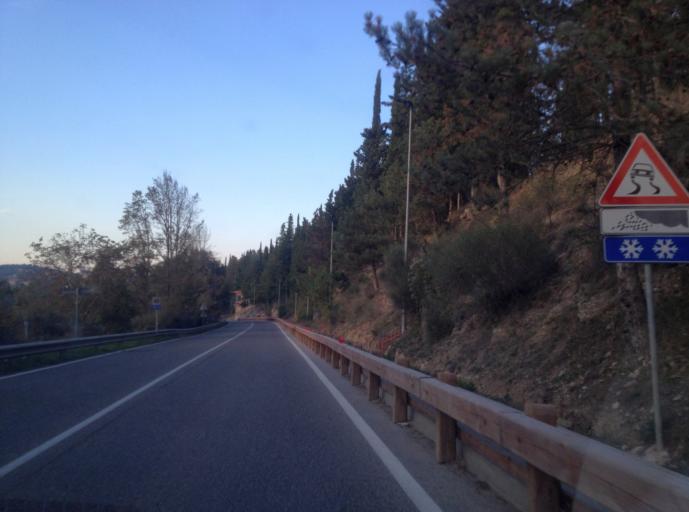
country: IT
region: Tuscany
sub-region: Provincia di Siena
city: Castellina in Chianti
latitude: 43.4572
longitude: 11.2923
